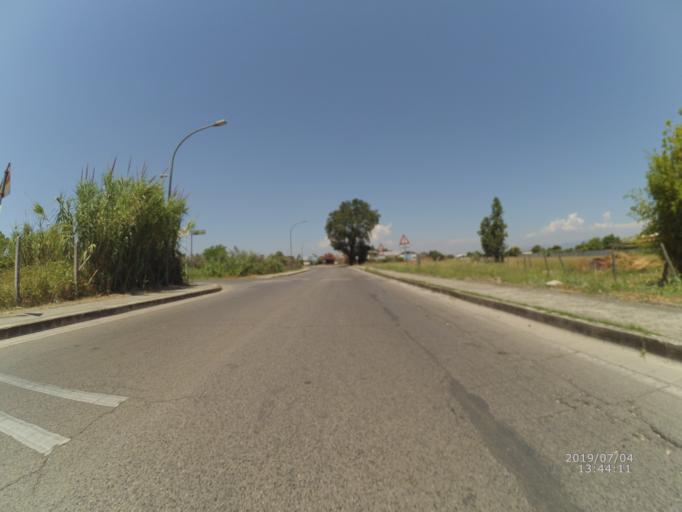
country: IT
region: Latium
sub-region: Provincia di Latina
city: San Felice Circeo
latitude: 41.2532
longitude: 13.0934
